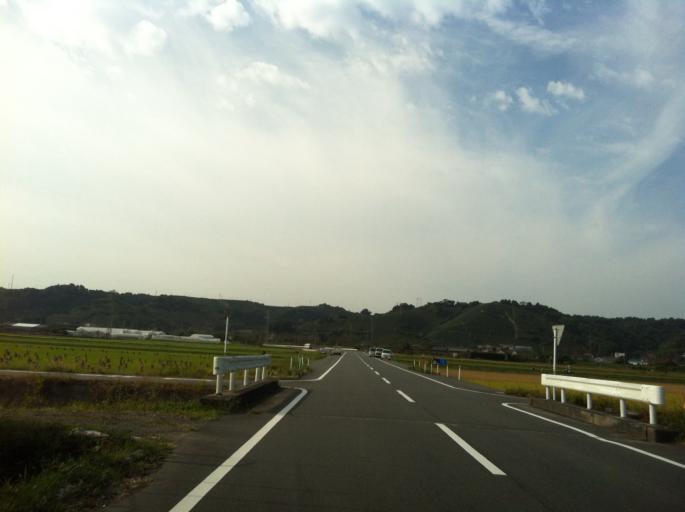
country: JP
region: Shizuoka
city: Sagara
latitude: 34.7526
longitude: 138.2074
